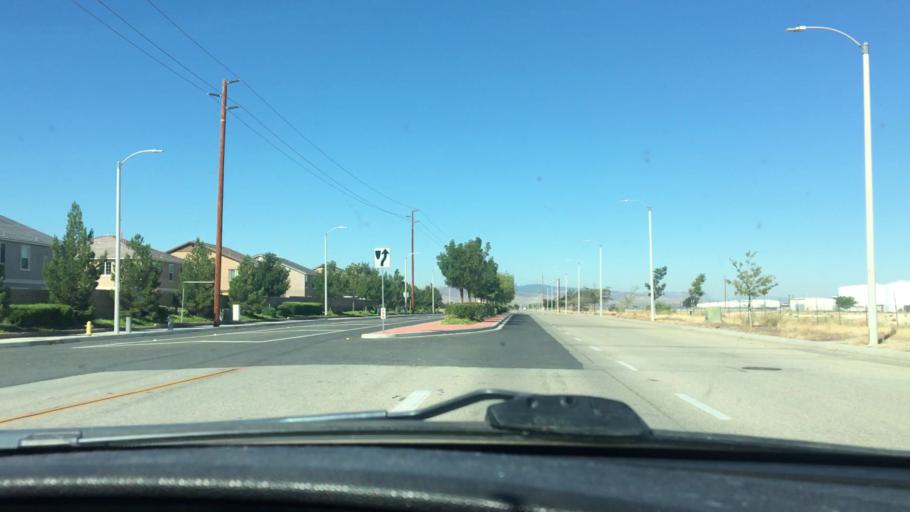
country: US
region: California
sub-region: Los Angeles County
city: Quartz Hill
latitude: 34.6895
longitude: -118.2234
